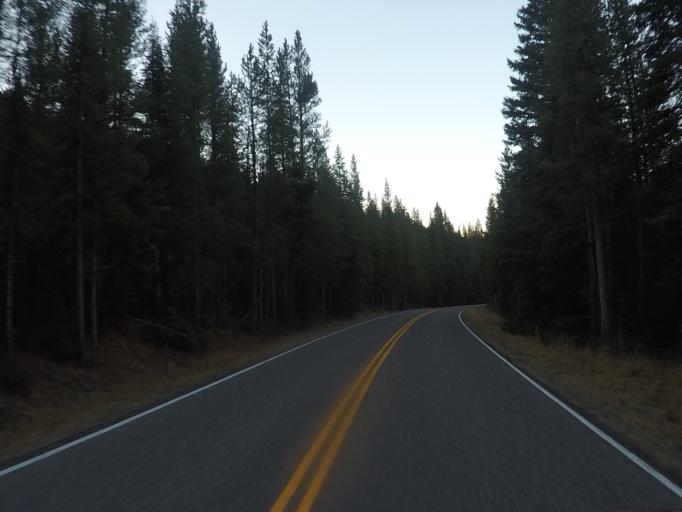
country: US
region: Montana
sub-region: Stillwater County
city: Absarokee
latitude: 44.9563
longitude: -110.0727
